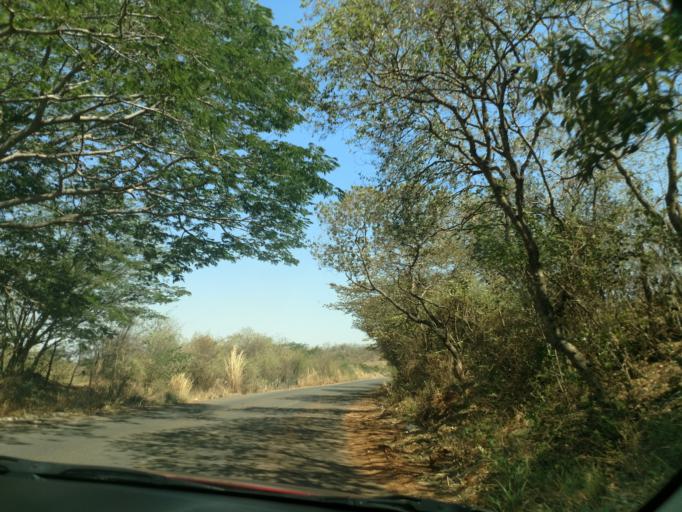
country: MX
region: Nayarit
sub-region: Tepic
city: La Corregidora
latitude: 21.4874
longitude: -104.6771
